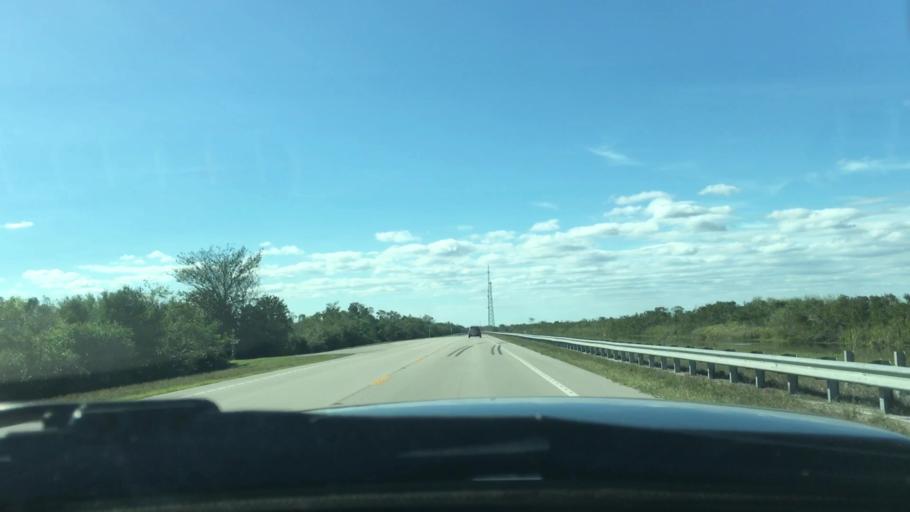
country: US
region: Florida
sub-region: Miami-Dade County
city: Kendall West
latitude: 25.7626
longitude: -80.8052
